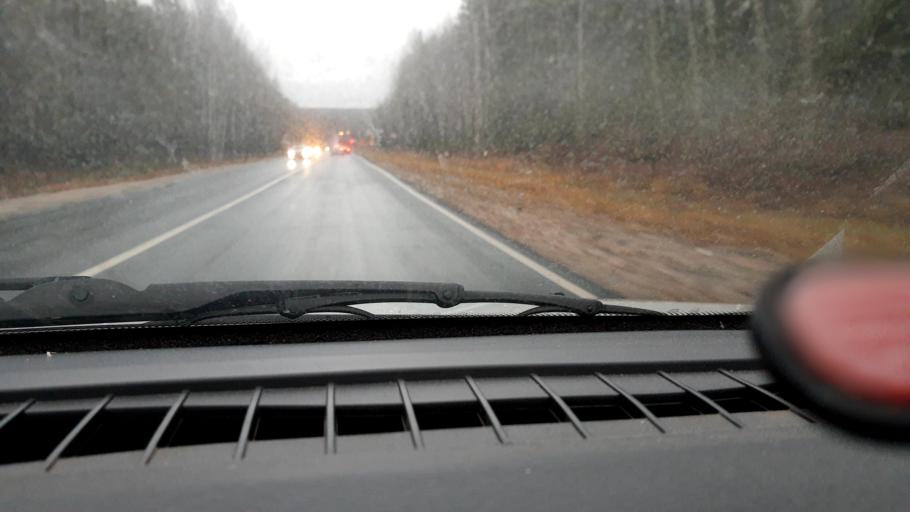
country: RU
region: Nizjnij Novgorod
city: Krasnyye Baki
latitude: 57.1035
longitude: 45.1843
